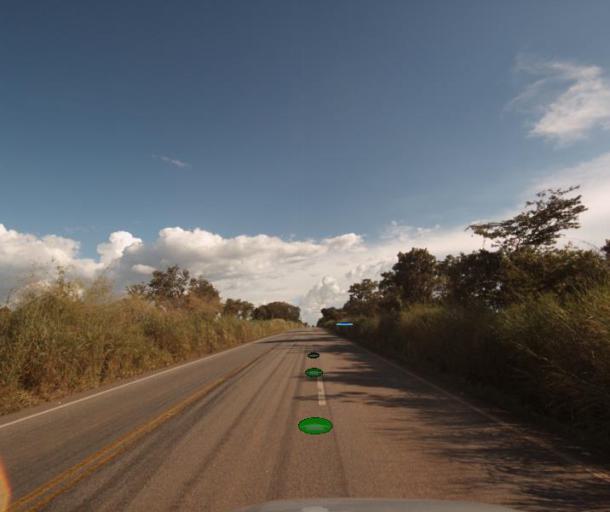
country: BR
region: Goias
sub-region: Porangatu
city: Porangatu
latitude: -13.0752
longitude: -49.1875
